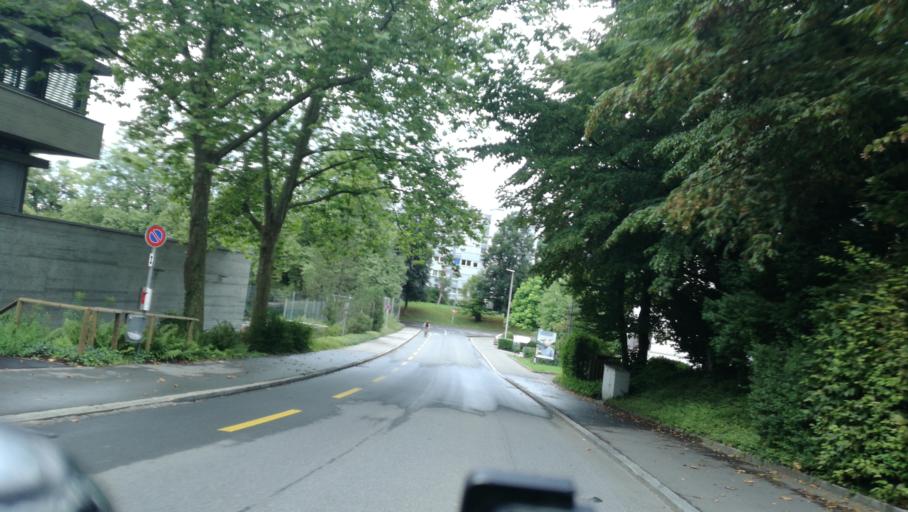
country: CH
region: Zug
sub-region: Zug
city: Zug
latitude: 47.1713
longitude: 8.5246
